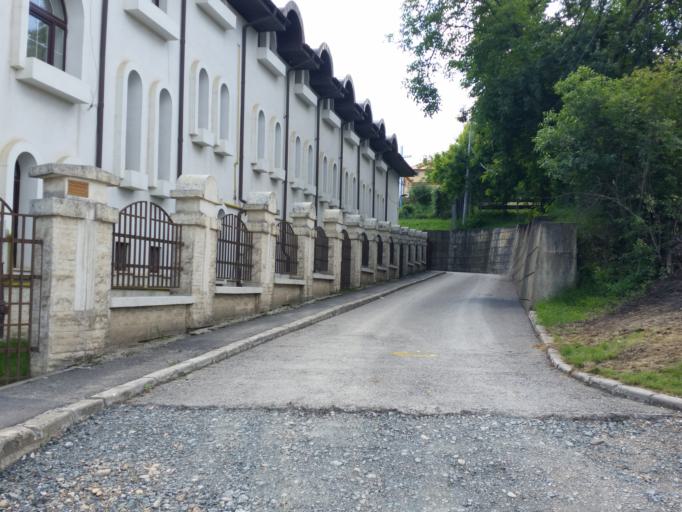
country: RO
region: Cluj
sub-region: Municipiul Cluj-Napoca
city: Cluj-Napoca
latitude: 46.7556
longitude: 23.6204
